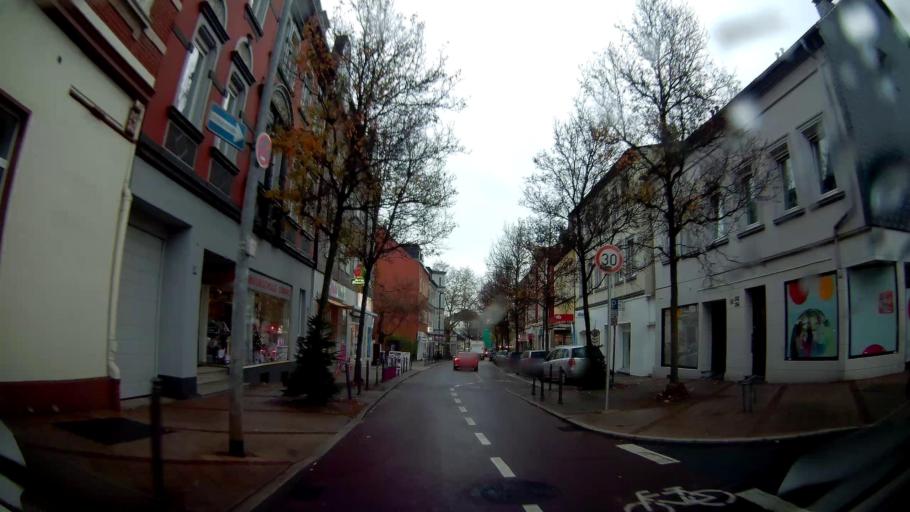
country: DE
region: North Rhine-Westphalia
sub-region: Regierungsbezirk Munster
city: Gelsenkirchen
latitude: 51.4679
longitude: 7.0808
